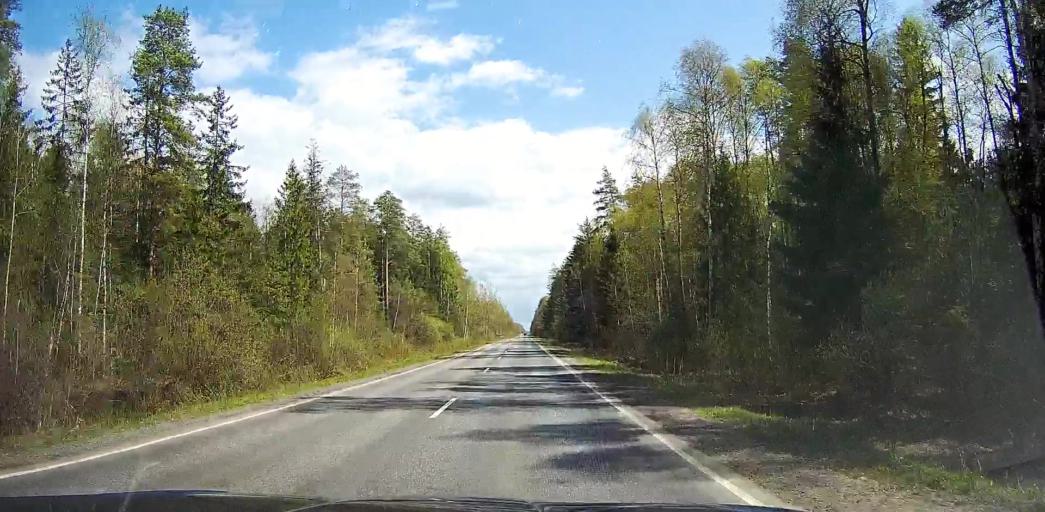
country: RU
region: Moskovskaya
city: Davydovo
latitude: 55.5515
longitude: 38.7586
